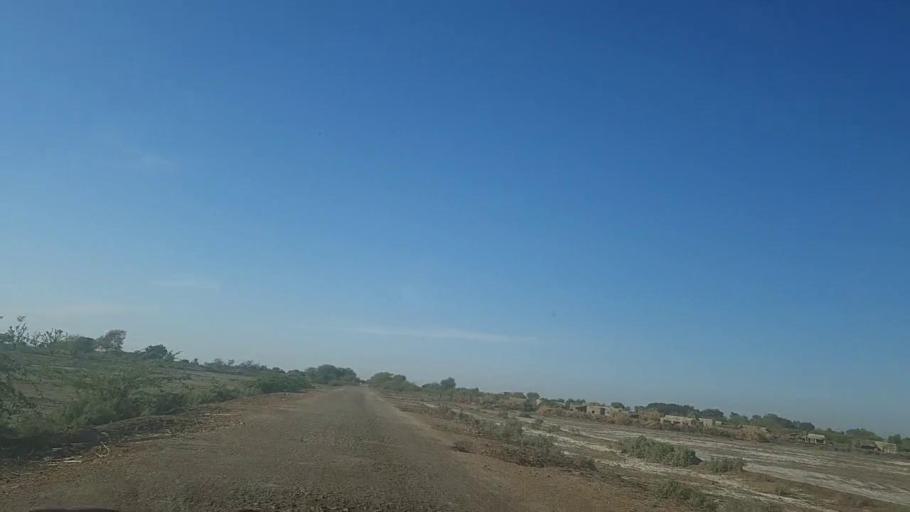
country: PK
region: Sindh
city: Pithoro
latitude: 25.5130
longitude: 69.3874
